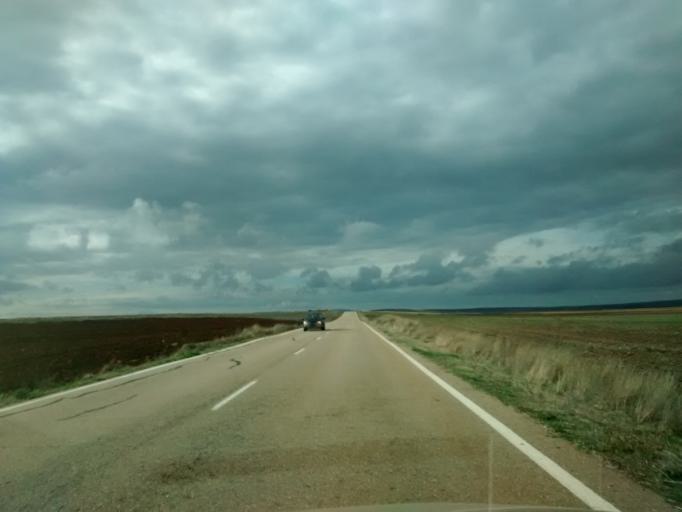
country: ES
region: Aragon
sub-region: Provincia de Zaragoza
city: Used
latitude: 40.9996
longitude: -1.5656
